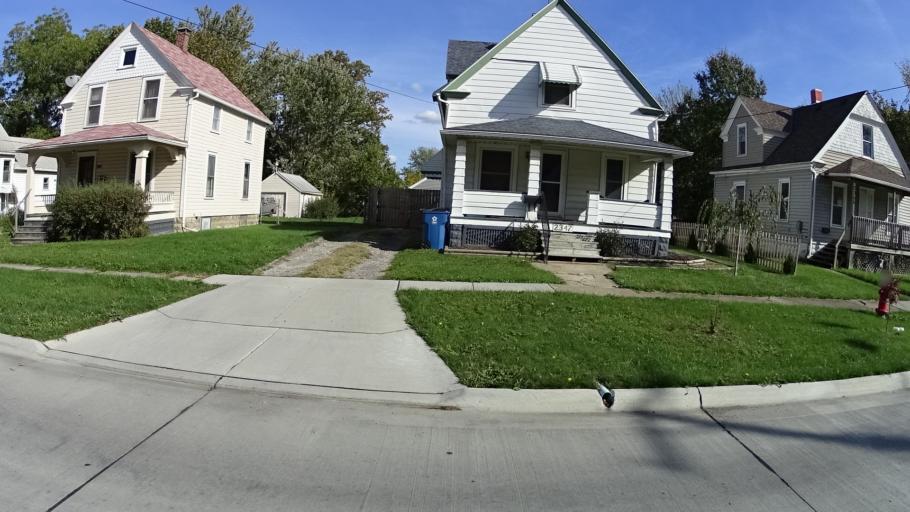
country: US
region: Ohio
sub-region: Lorain County
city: Lorain
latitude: 41.4486
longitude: -82.1684
